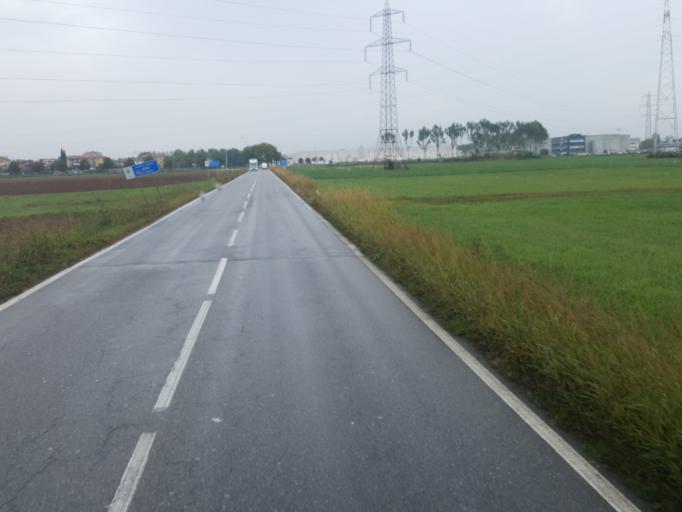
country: IT
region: Lombardy
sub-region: Provincia di Varese
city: Origgio
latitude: 45.5861
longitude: 9.0245
